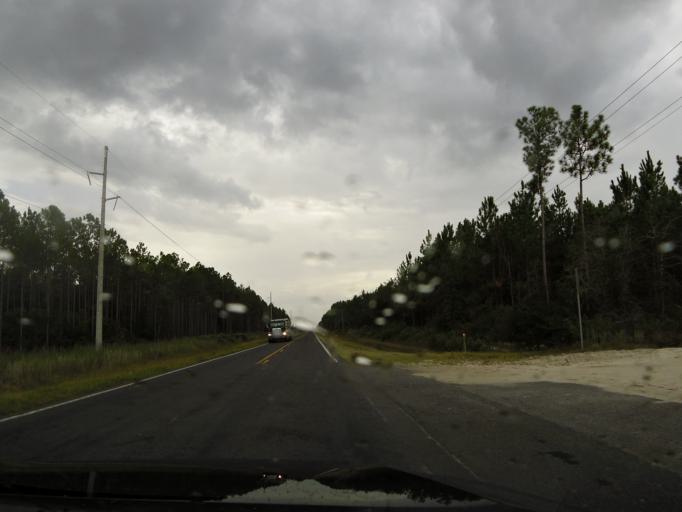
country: US
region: Florida
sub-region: Nassau County
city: Hilliard
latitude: 30.5655
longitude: -82.0437
